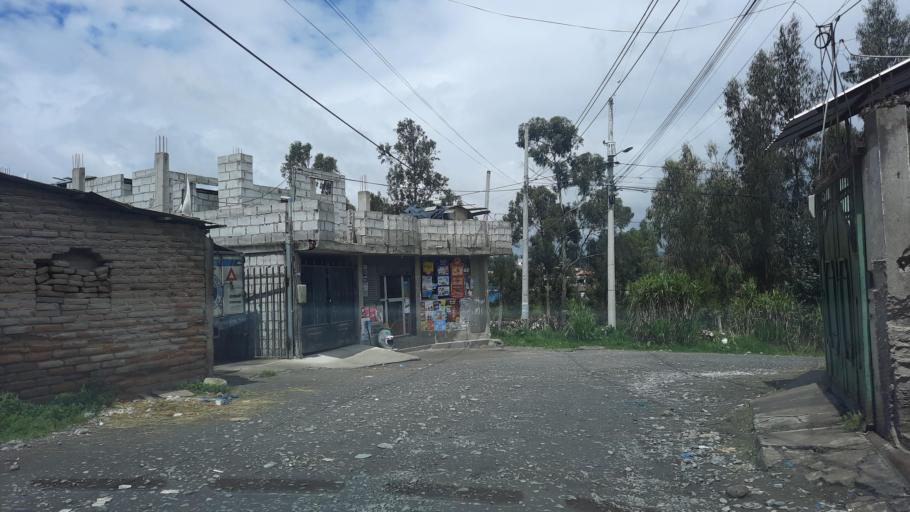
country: EC
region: Chimborazo
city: Riobamba
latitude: -1.6857
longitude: -78.6660
